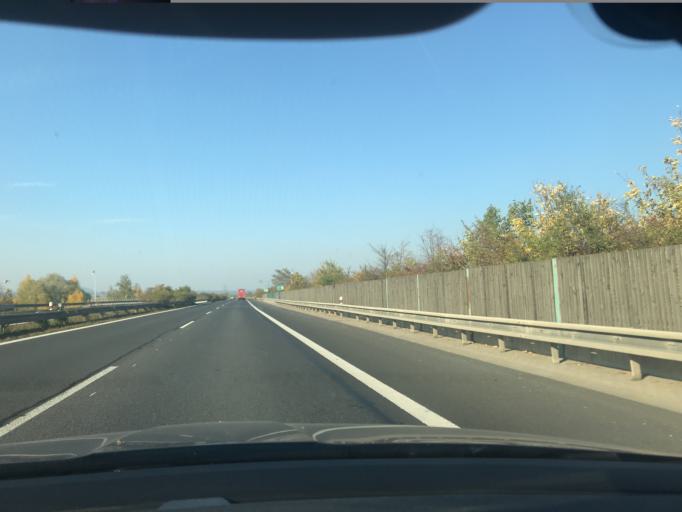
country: CZ
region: Central Bohemia
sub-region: Okres Melnik
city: Veltrusy
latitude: 50.2552
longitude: 14.3711
